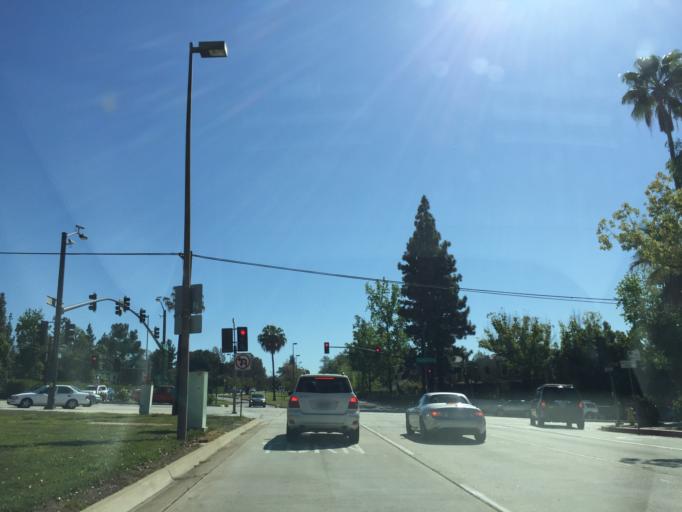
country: US
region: California
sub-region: Los Angeles County
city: East Pasadena
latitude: 34.1615
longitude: -118.0818
